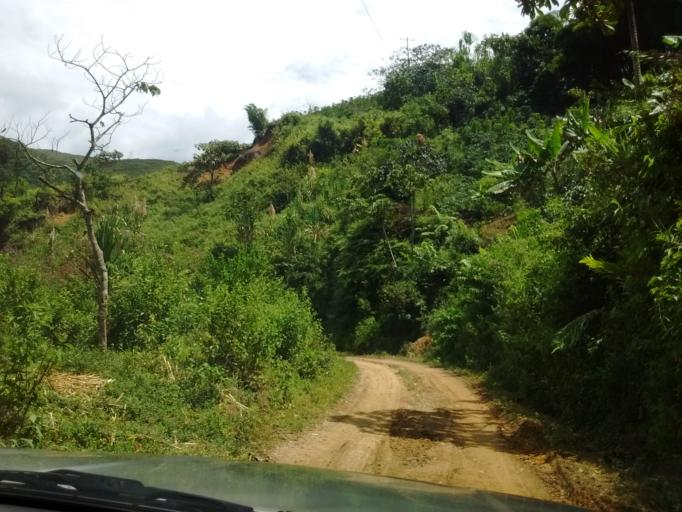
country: CO
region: Cauca
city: Morales
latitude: 2.6704
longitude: -76.7645
